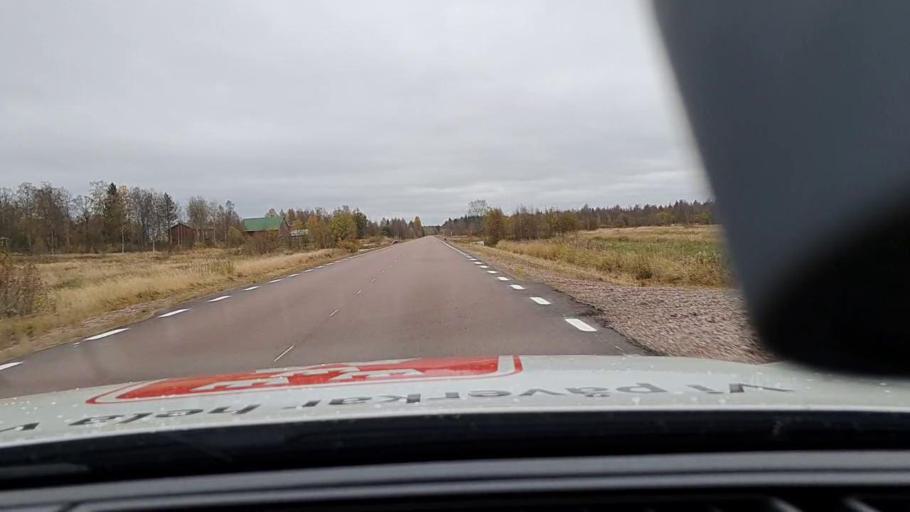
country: FI
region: Lapland
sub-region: Kemi-Tornio
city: Tornio
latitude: 66.0593
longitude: 23.9284
